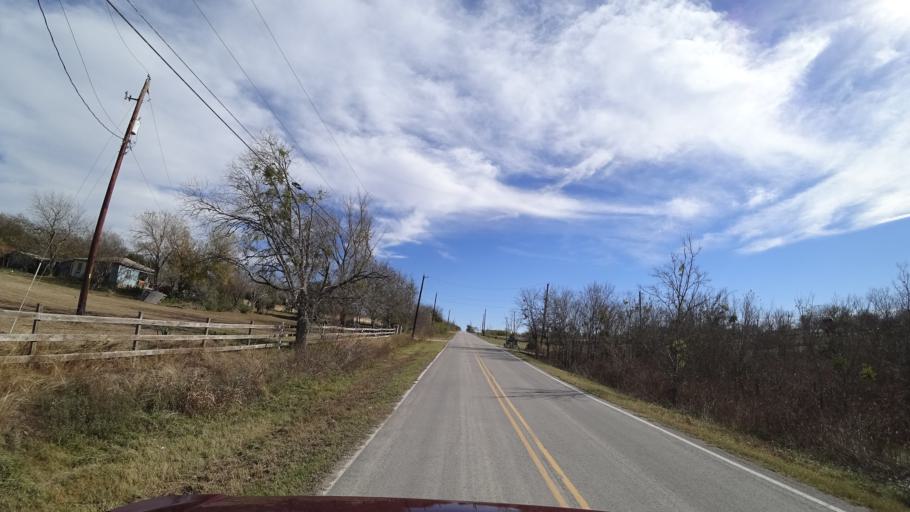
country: US
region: Texas
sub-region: Travis County
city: Onion Creek
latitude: 30.1226
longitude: -97.7375
